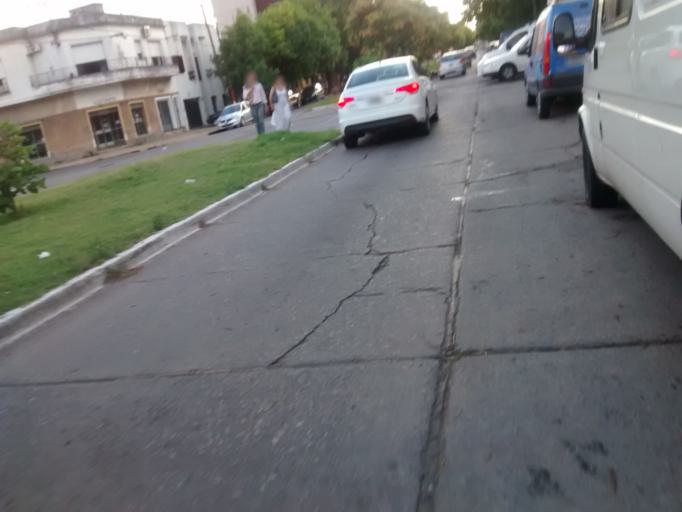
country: AR
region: Buenos Aires
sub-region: Partido de La Plata
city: La Plata
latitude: -34.9119
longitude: -57.9690
